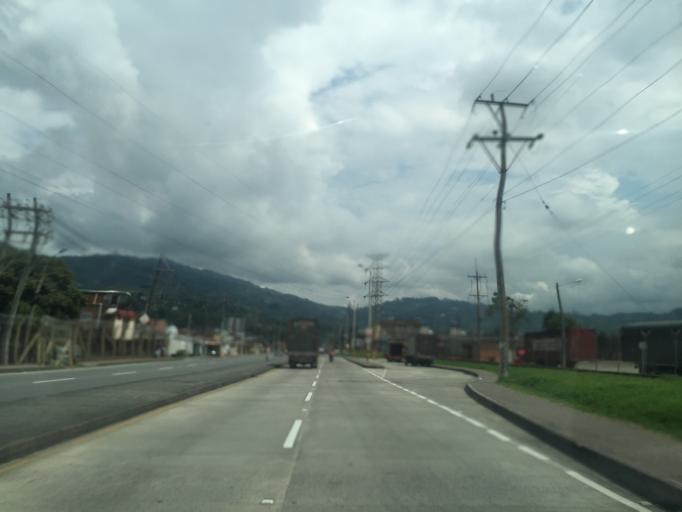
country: CO
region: Risaralda
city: Dos Quebradas
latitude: 4.8354
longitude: -75.6777
